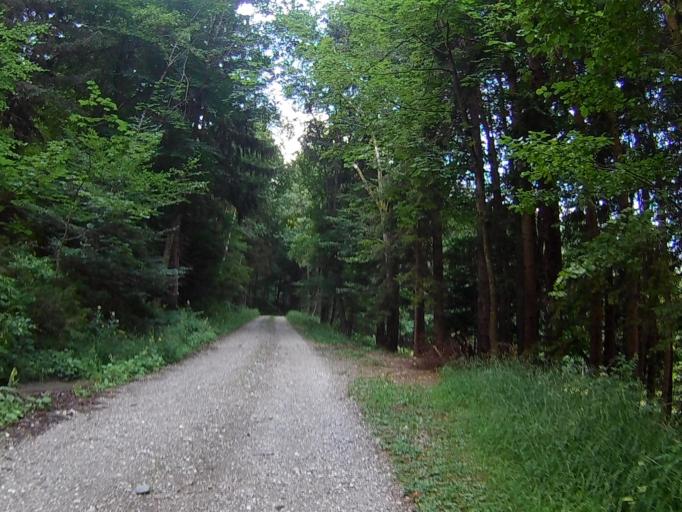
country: SI
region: Selnica ob Dravi
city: Selnica ob Dravi
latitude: 46.5185
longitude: 15.4705
